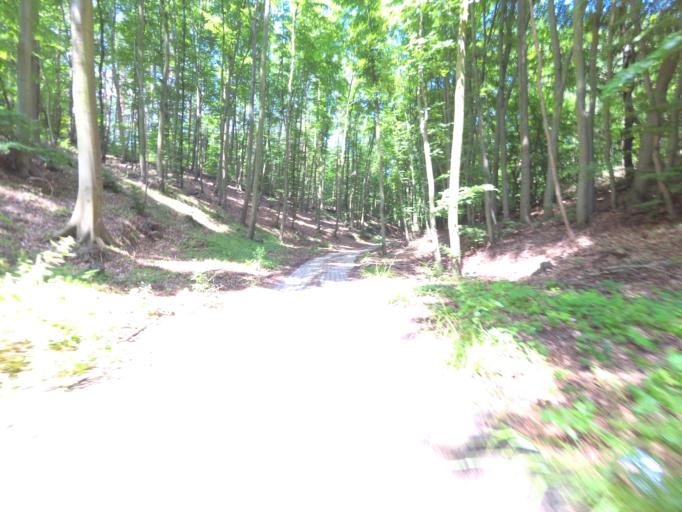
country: PL
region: Pomeranian Voivodeship
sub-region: Gdynia
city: Wielki Kack
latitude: 54.4872
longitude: 18.5082
